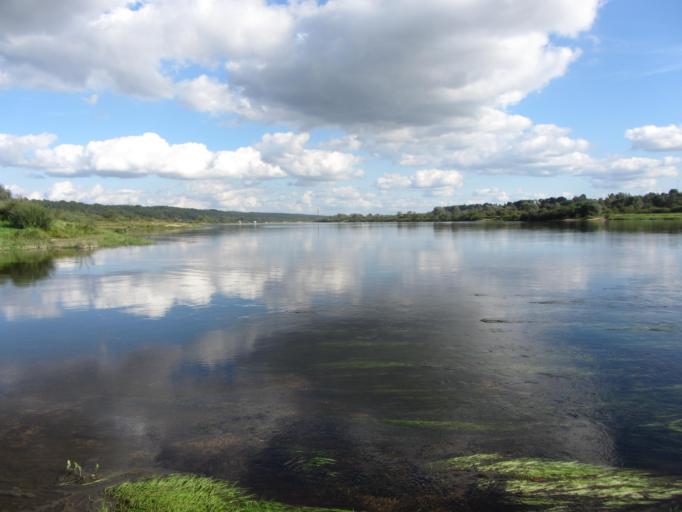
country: LT
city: Vilkija
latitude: 55.0751
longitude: 23.4135
